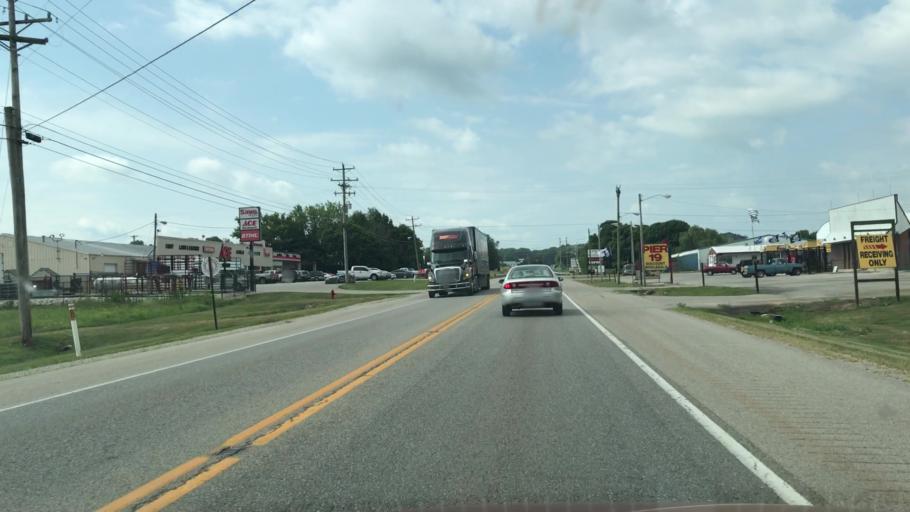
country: US
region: Kentucky
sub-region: Barren County
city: Cave City
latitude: 37.1245
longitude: -85.9615
